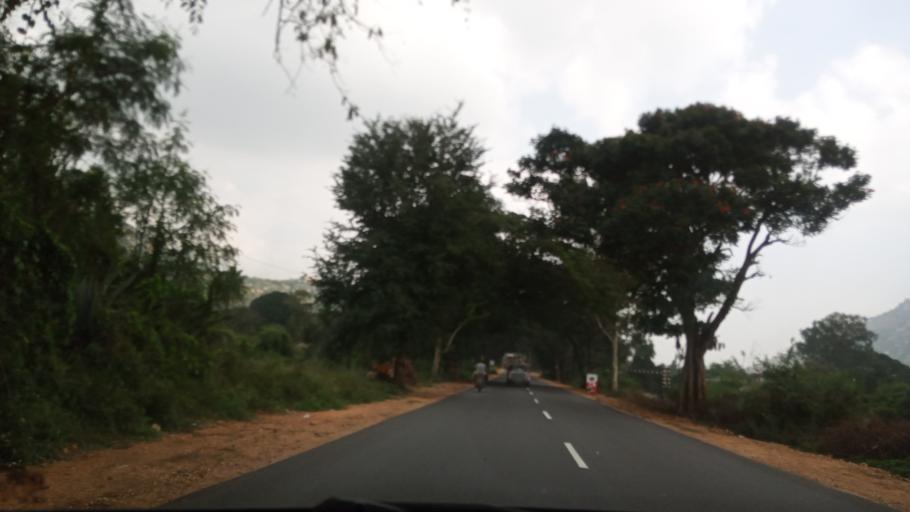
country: IN
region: Andhra Pradesh
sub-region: Chittoor
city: Madanapalle
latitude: 13.6365
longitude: 78.5850
